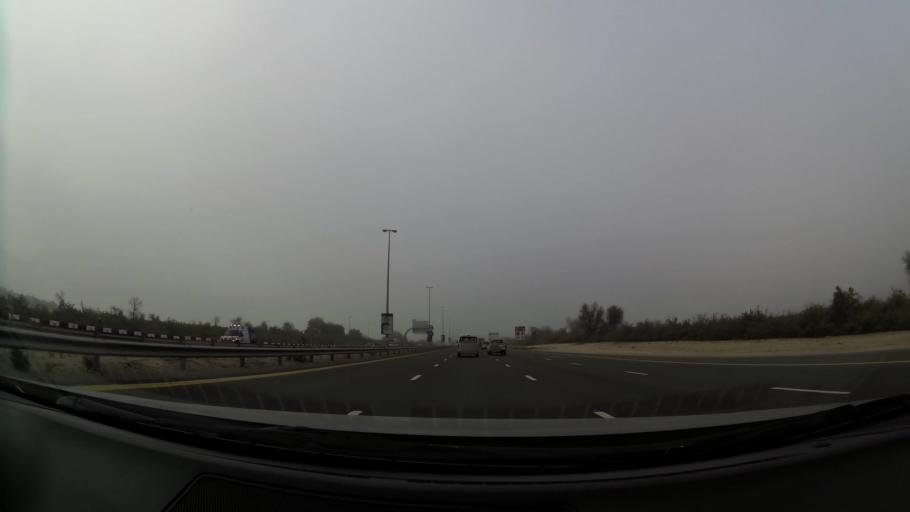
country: AE
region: Dubai
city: Dubai
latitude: 25.1634
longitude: 55.3295
